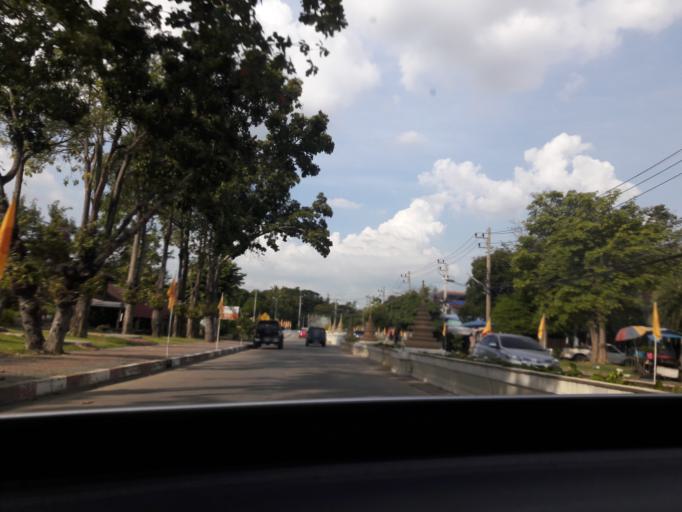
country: TH
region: Sing Buri
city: Sing Buri
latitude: 14.8533
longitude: 100.3887
